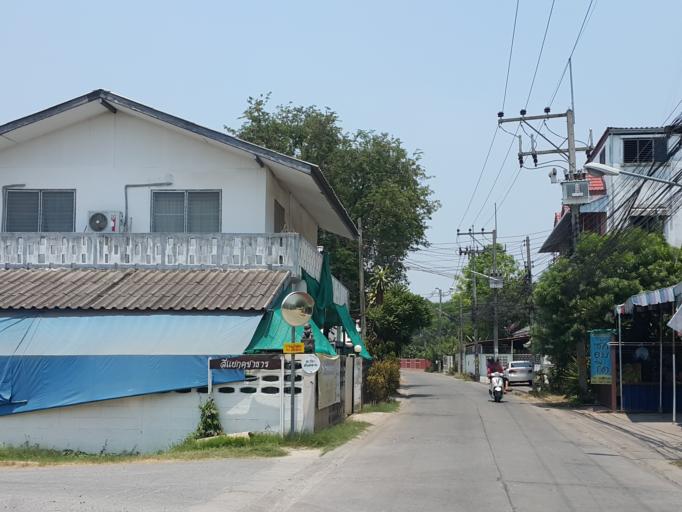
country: TH
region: Phitsanulok
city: Phitsanulok
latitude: 16.8149
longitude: 100.2547
